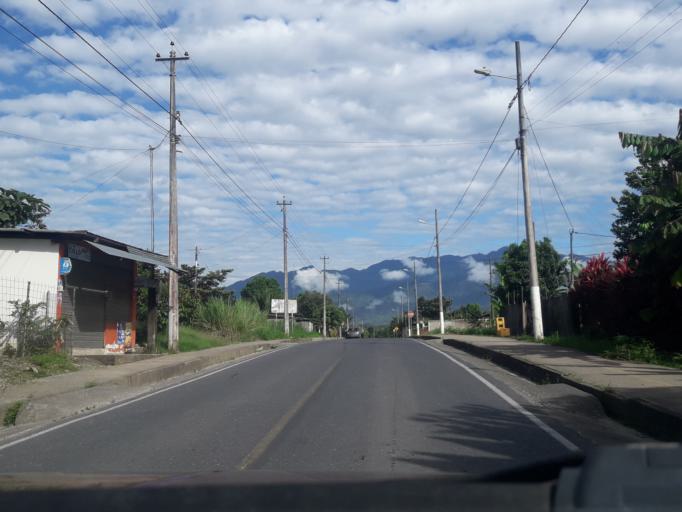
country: EC
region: Napo
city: Tena
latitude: -0.9849
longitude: -77.8377
